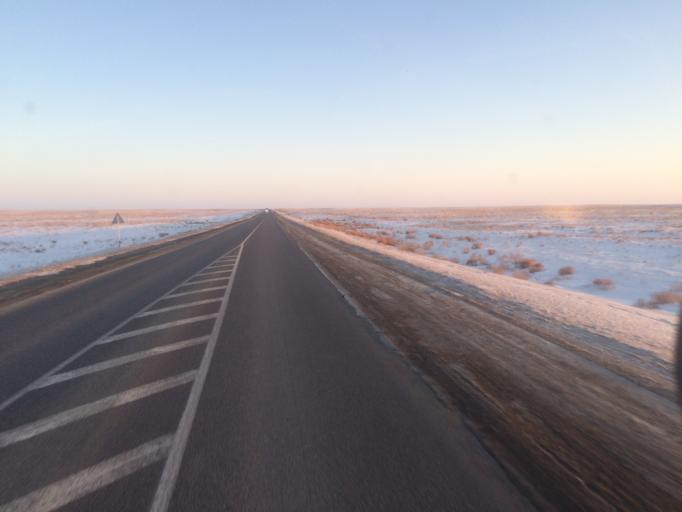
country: KZ
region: Qyzylorda
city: Sekseuil
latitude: 47.6798
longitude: 61.4421
